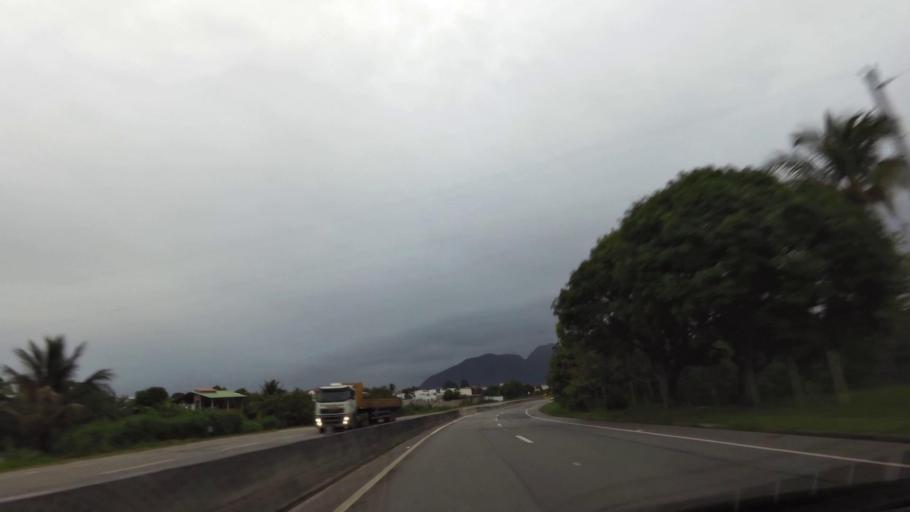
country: BR
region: Espirito Santo
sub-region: Guarapari
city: Guarapari
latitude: -20.6140
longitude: -40.4525
